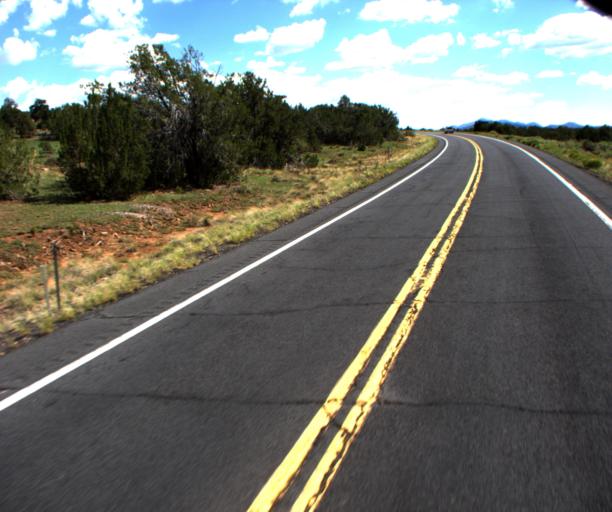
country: US
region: Arizona
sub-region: Coconino County
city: Williams
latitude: 35.4782
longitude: -112.1775
